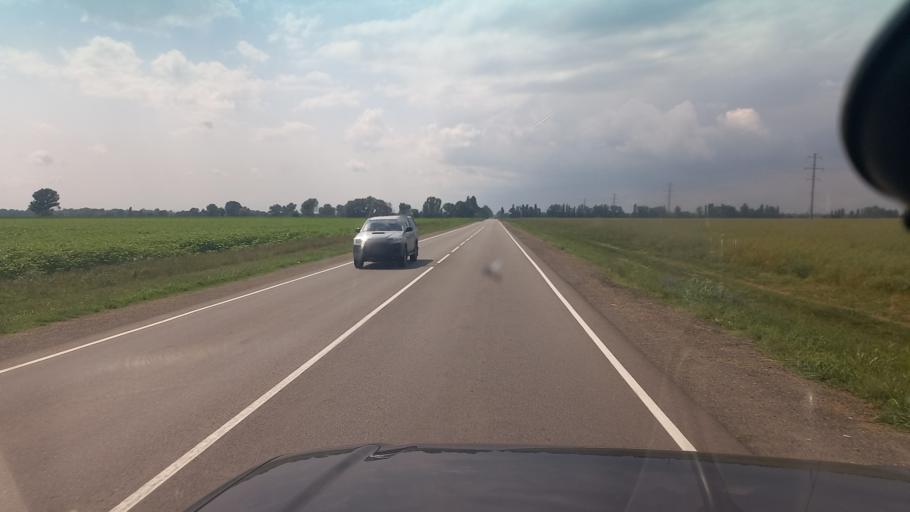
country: RU
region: Adygeya
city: Koshekhabl'
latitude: 44.9081
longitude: 40.4573
